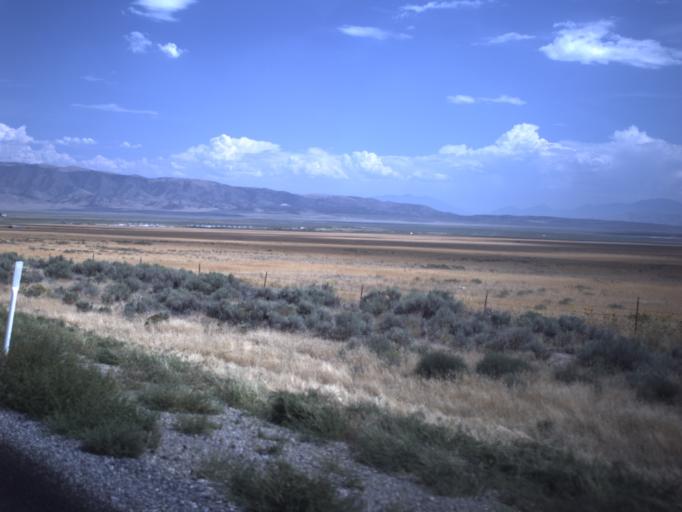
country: US
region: Utah
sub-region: Utah County
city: Eagle Mountain
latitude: 40.2454
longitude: -112.1361
